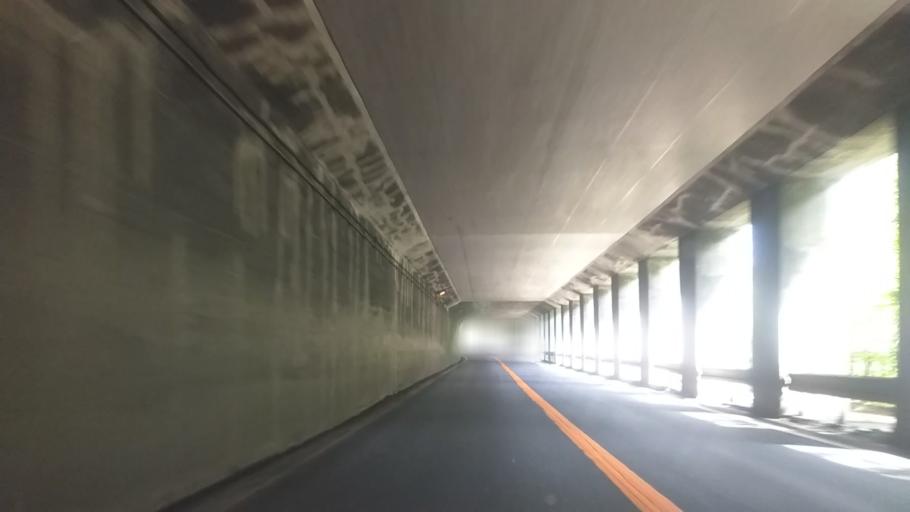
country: JP
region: Nagano
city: Saku
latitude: 36.0511
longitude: 138.4707
